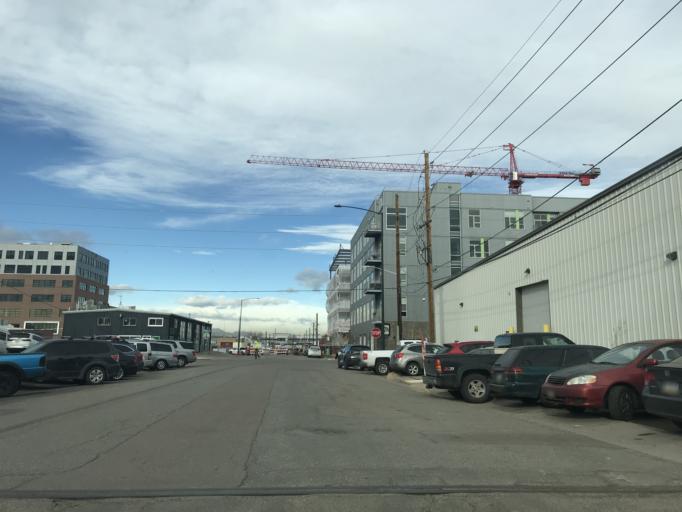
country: US
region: Colorado
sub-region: Denver County
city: Denver
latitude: 39.7703
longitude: -104.9763
